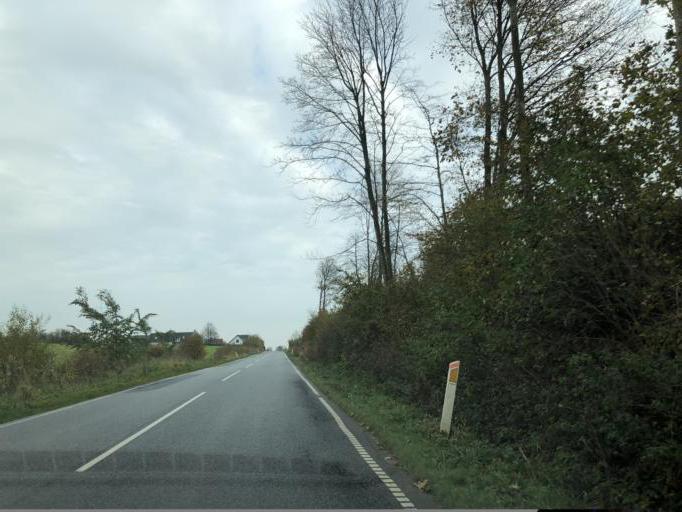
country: DK
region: Central Jutland
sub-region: Hedensted Kommune
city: Hedensted
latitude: 55.7356
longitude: 9.7555
